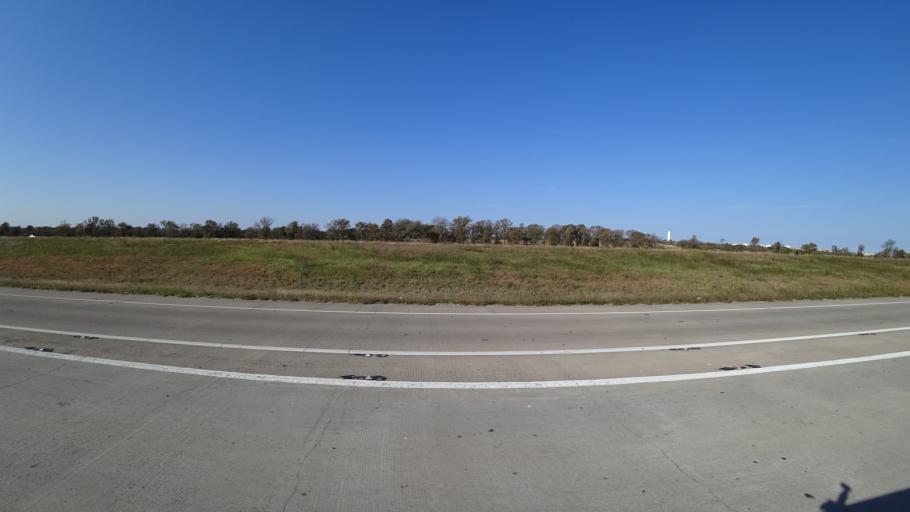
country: US
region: Texas
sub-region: Travis County
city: Pflugerville
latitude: 30.4457
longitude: -97.5940
